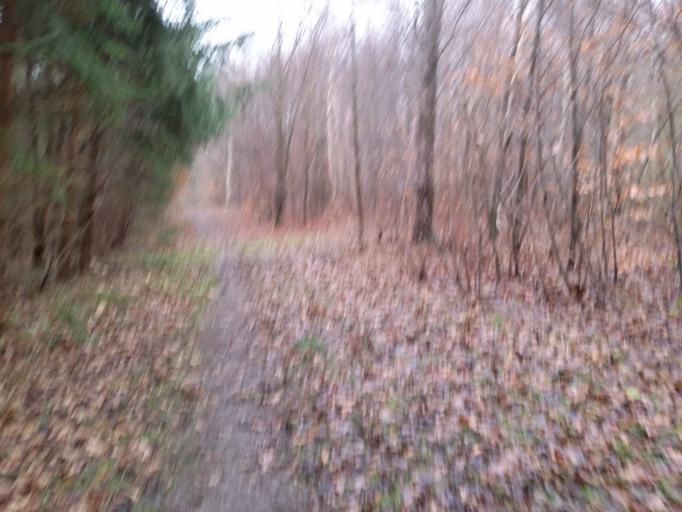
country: DK
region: Capital Region
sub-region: Frederikssund Kommune
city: Slangerup
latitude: 55.8388
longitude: 12.1920
